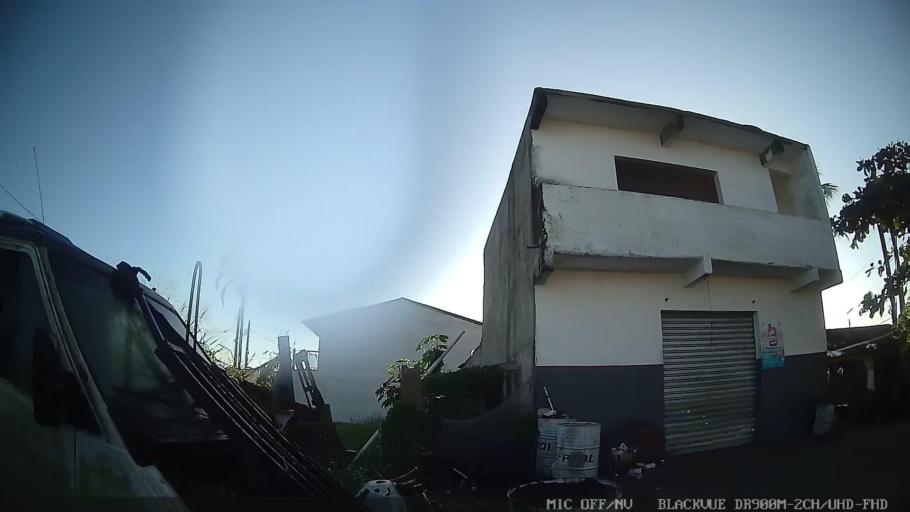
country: BR
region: Sao Paulo
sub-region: Itanhaem
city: Itanhaem
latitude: -24.2324
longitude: -46.9021
